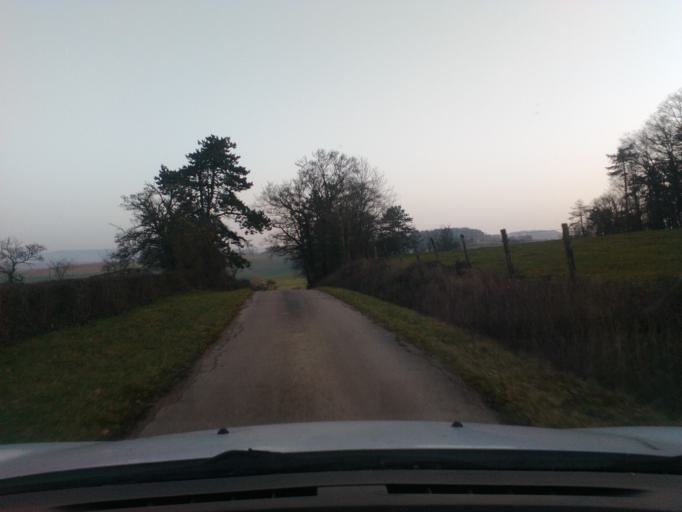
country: FR
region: Lorraine
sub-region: Departement des Vosges
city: Vittel
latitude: 48.2579
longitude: 5.9998
